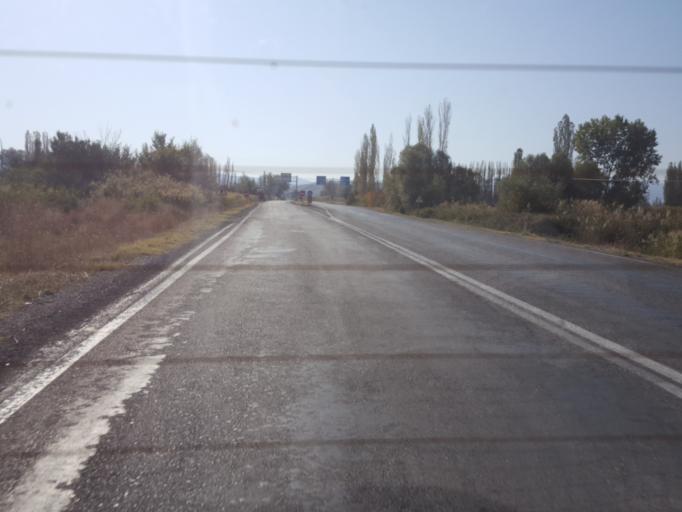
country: TR
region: Corum
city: Seydim
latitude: 40.5969
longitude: 34.5914
